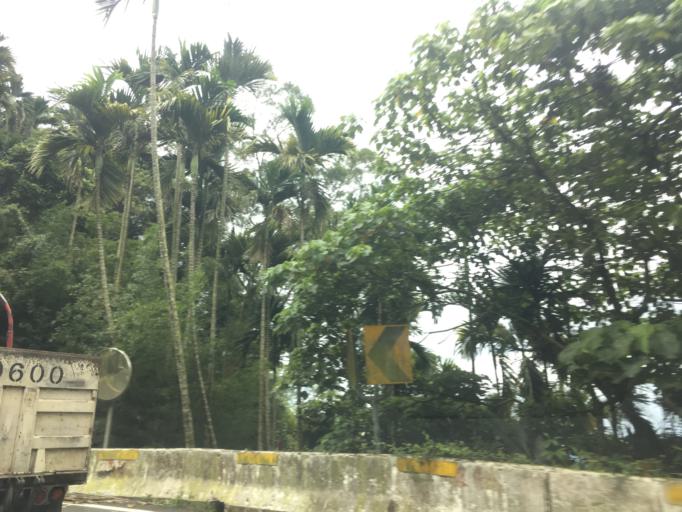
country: TW
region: Taiwan
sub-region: Yunlin
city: Douliu
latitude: 23.5592
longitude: 120.5841
